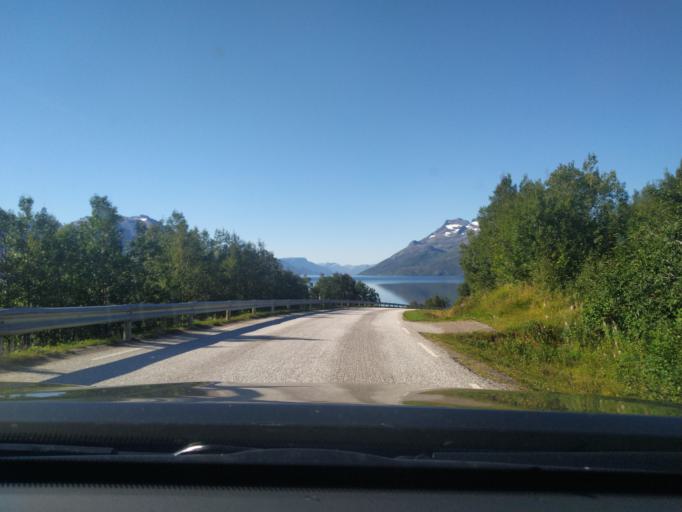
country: NO
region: Troms
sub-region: Dyroy
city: Brostadbotn
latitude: 68.9239
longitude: 17.6374
